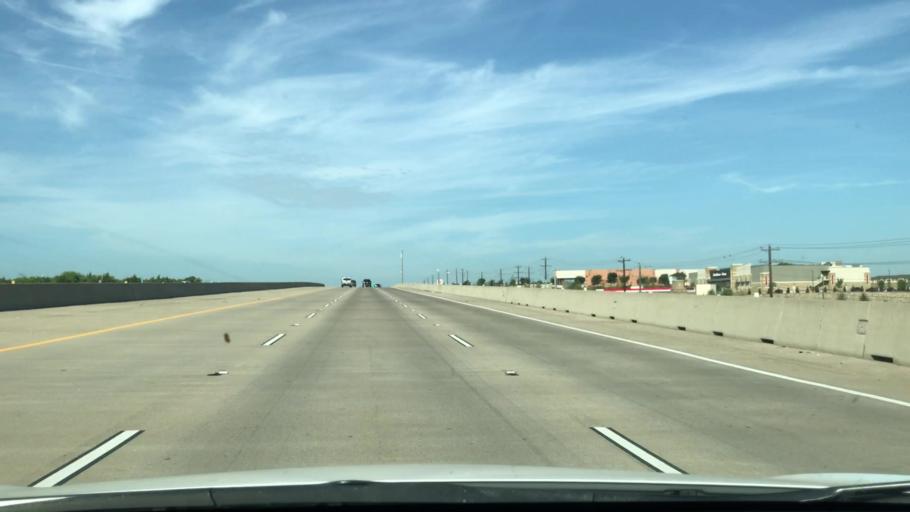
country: US
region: Texas
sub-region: Collin County
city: Allen
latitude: 33.1300
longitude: -96.7195
